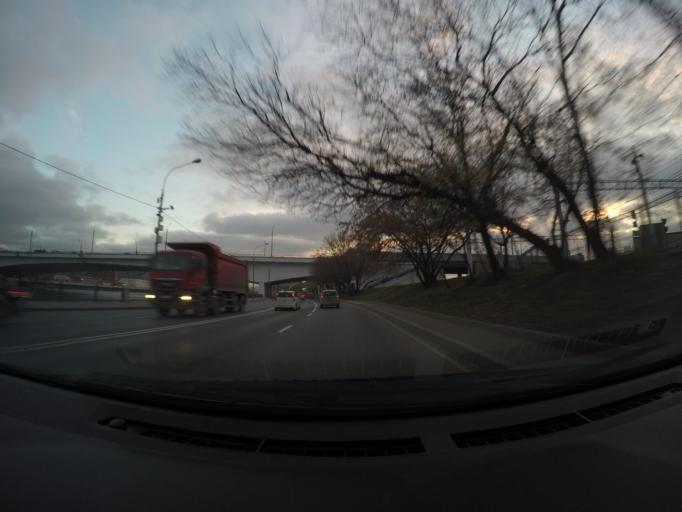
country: RU
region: Moscow
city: Zamoskvorech'ye
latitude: 55.7064
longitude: 37.6274
